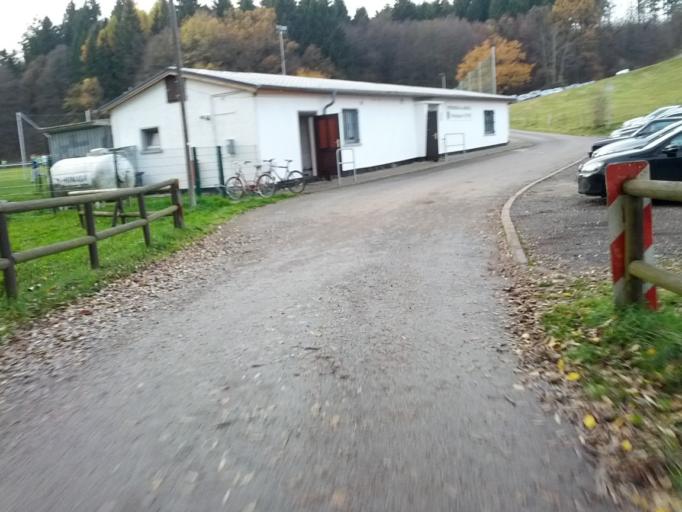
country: DE
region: Thuringia
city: Ruhla
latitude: 50.9346
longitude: 10.3454
